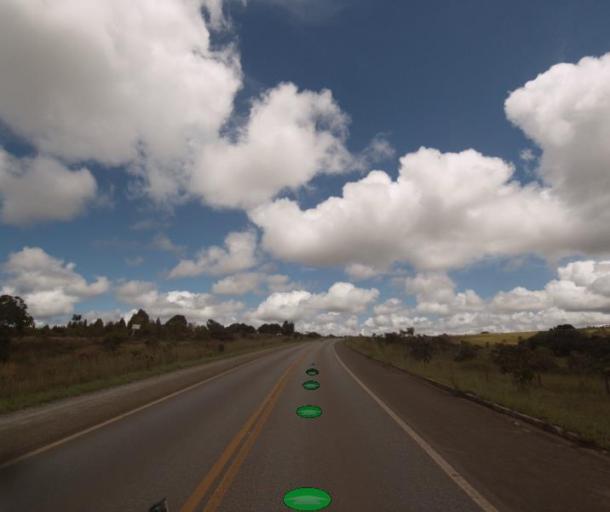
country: BR
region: Goias
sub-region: Abadiania
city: Abadiania
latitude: -15.7825
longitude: -48.4737
